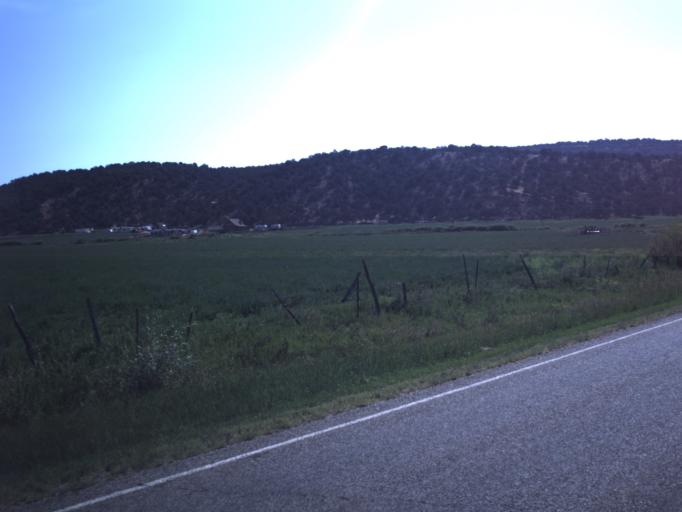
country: US
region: Utah
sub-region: Duchesne County
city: Duchesne
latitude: 40.3356
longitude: -110.6800
